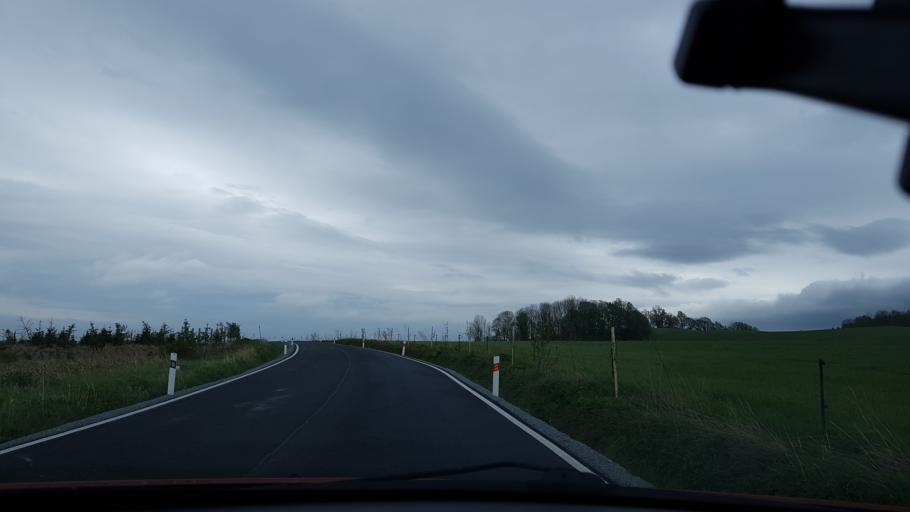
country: PL
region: Opole Voivodeship
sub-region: Powiat nyski
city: Kamienica
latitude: 50.4354
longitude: 16.9379
